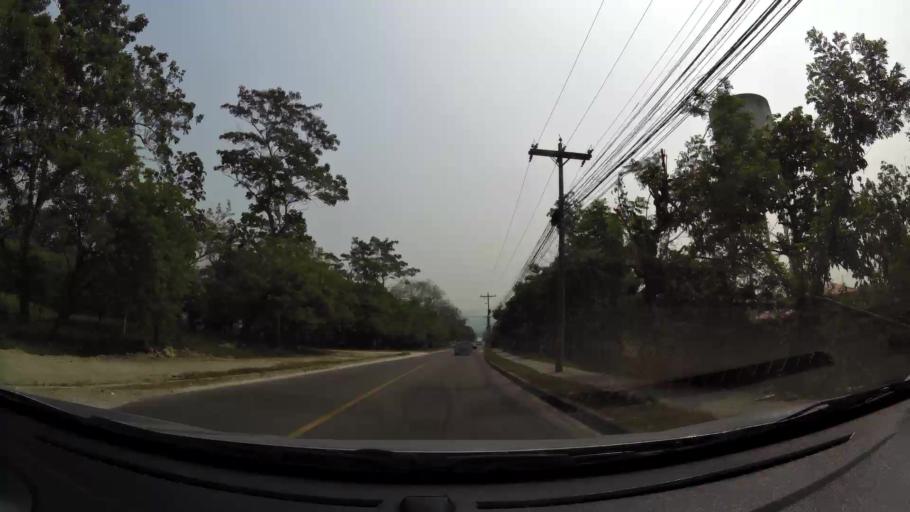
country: HN
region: Cortes
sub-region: San Pedro Sula
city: Pena Blanca
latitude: 15.5636
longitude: -88.0305
